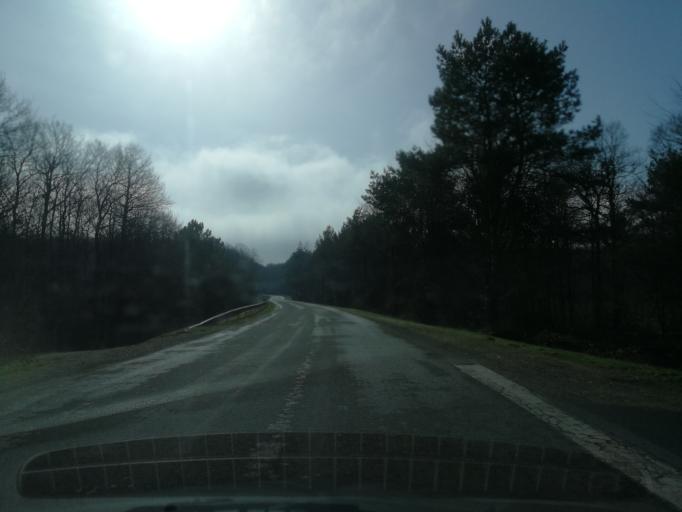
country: FR
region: Brittany
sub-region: Departement du Morbihan
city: Serent
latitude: 47.7622
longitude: -2.5168
